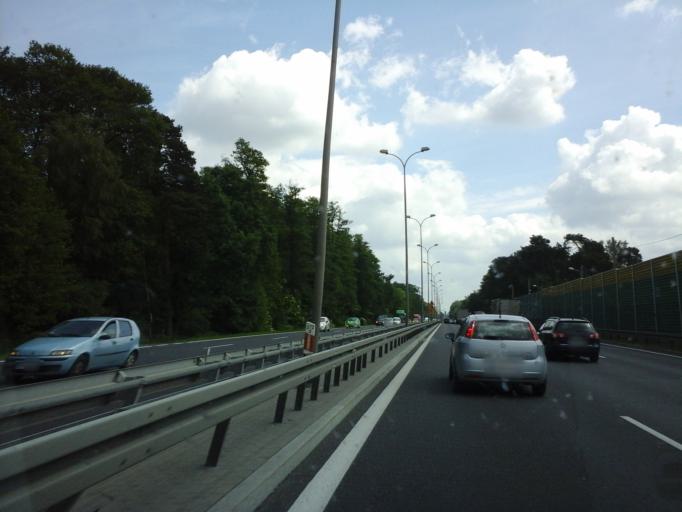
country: PL
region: Lodz Voivodeship
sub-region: Powiat lodzki wschodni
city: Tuszyn
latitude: 51.6205
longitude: 19.5183
